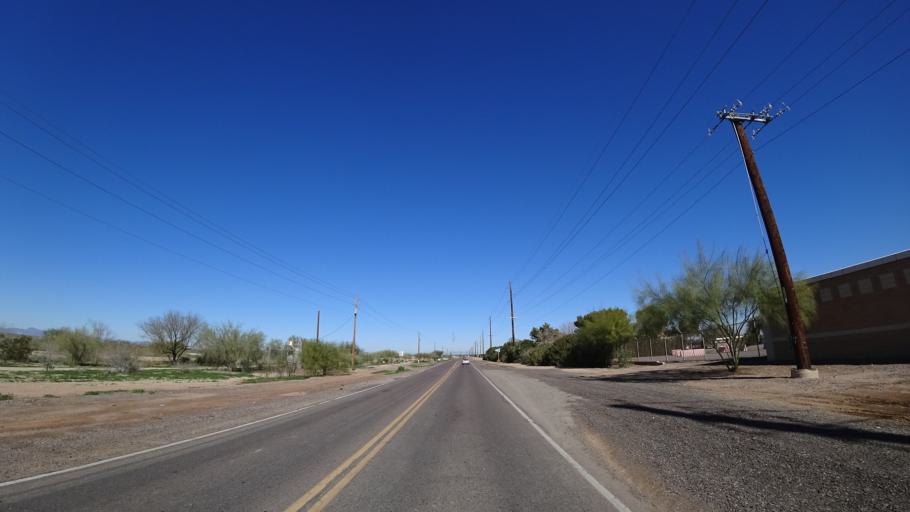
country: US
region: Arizona
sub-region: Maricopa County
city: Tolleson
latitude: 33.3930
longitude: -112.2543
